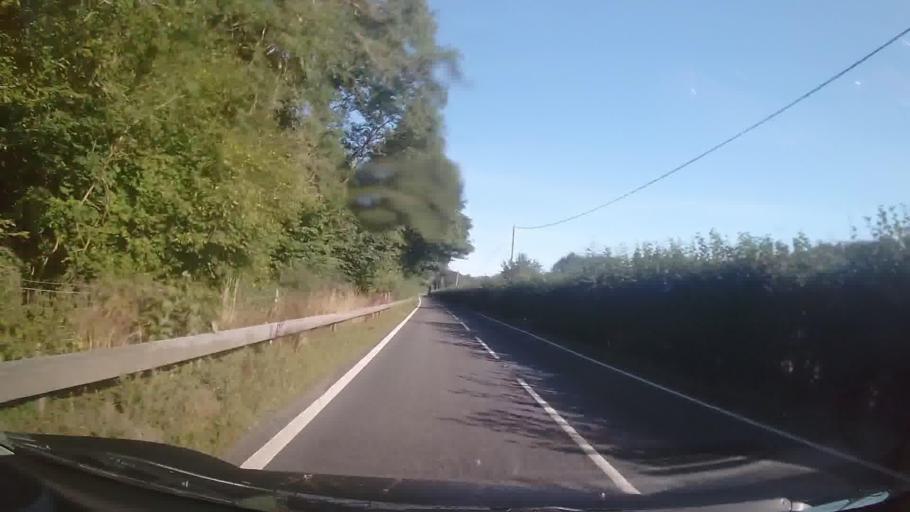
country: GB
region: Wales
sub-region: Blaenau Gwent
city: Brynmawr
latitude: 51.9230
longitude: -3.1870
